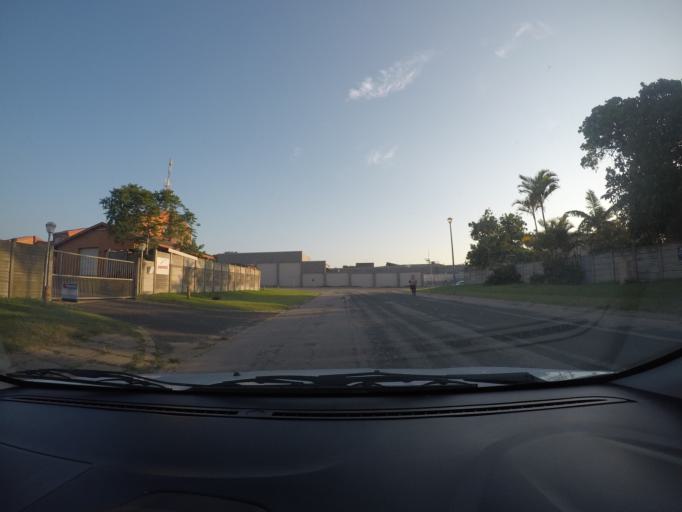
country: ZA
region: KwaZulu-Natal
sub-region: uThungulu District Municipality
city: Richards Bay
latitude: -28.7806
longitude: 32.1008
